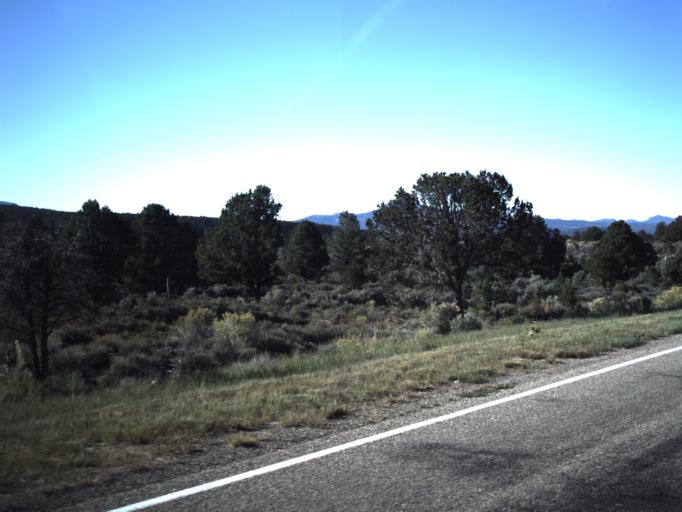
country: US
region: Utah
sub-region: Garfield County
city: Panguitch
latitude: 37.7884
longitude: -112.4395
